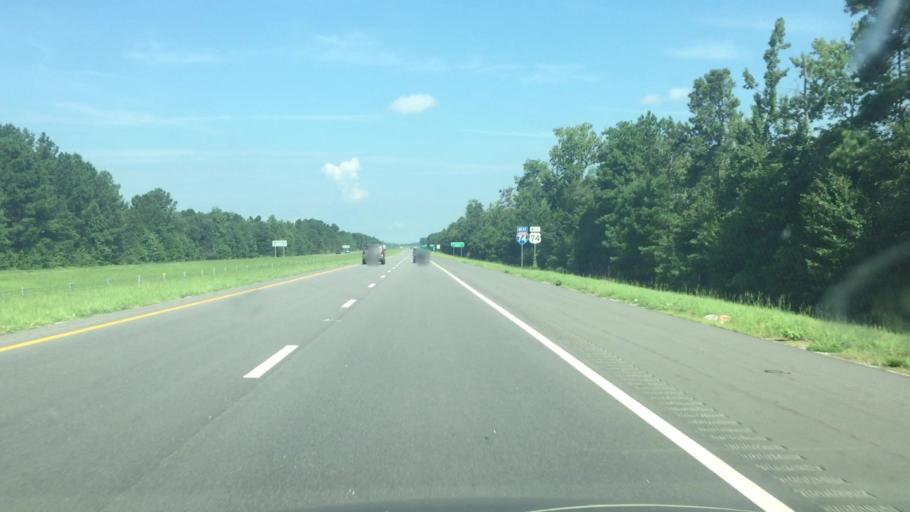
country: US
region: North Carolina
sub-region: Robeson County
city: Pembroke
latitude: 34.6573
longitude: -79.2510
